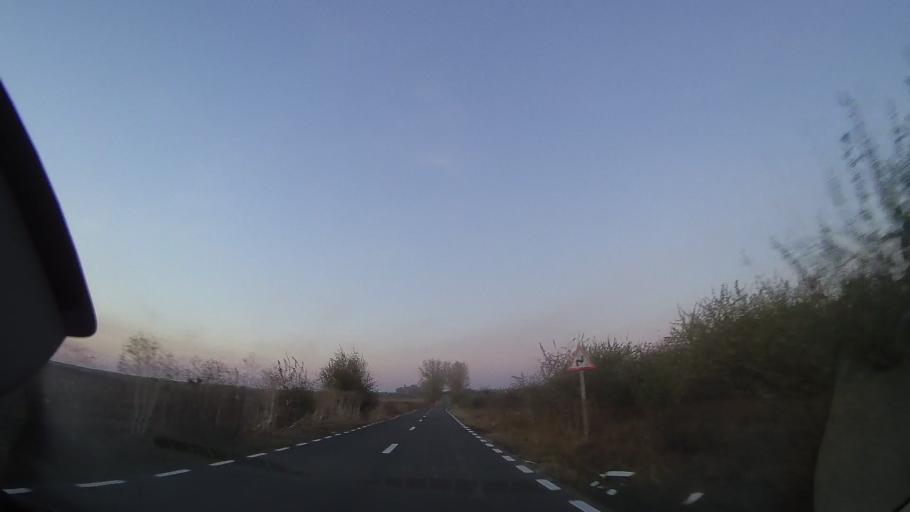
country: RO
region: Constanta
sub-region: Comuna Cobadin
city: Cobadin
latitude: 44.0367
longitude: 28.2590
